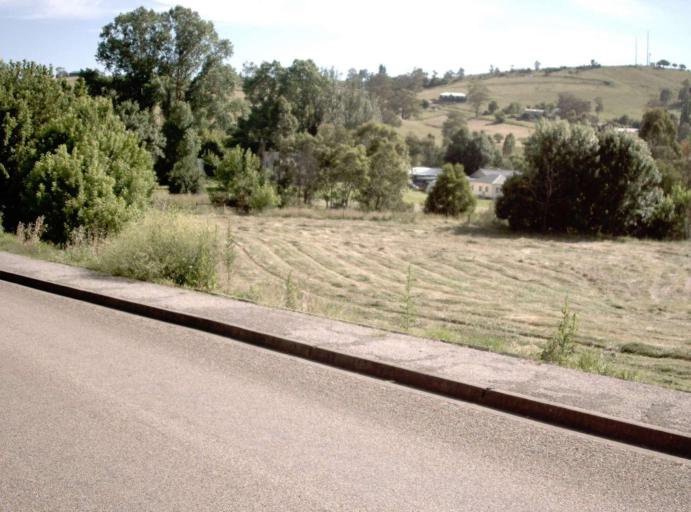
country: AU
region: Victoria
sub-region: East Gippsland
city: Lakes Entrance
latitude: -37.4978
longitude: 148.1730
